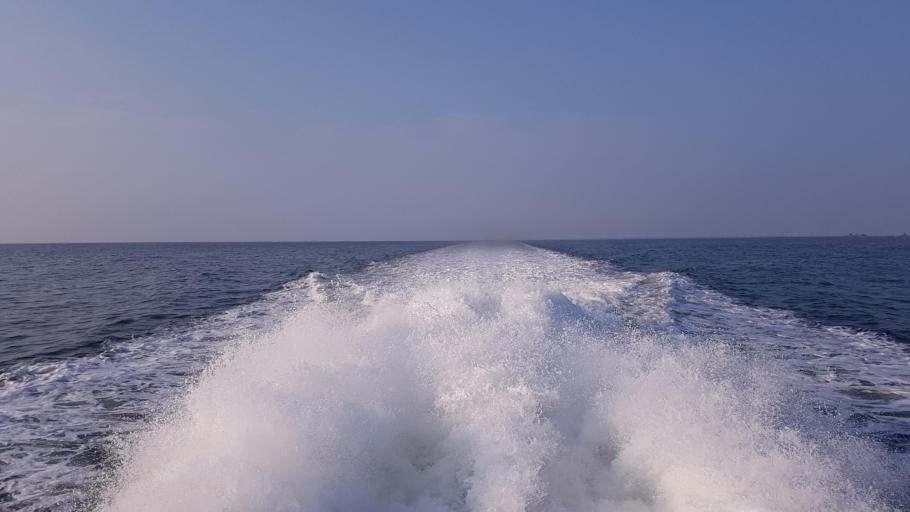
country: DE
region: Schleswig-Holstein
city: Pellworm
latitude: 54.5308
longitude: 8.7501
